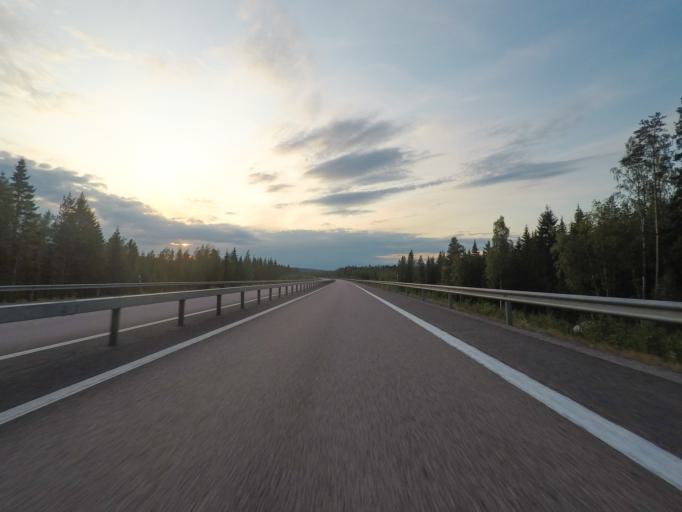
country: FI
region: Central Finland
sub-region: Jyvaeskylae
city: Toivakka
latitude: 62.1163
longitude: 25.9650
